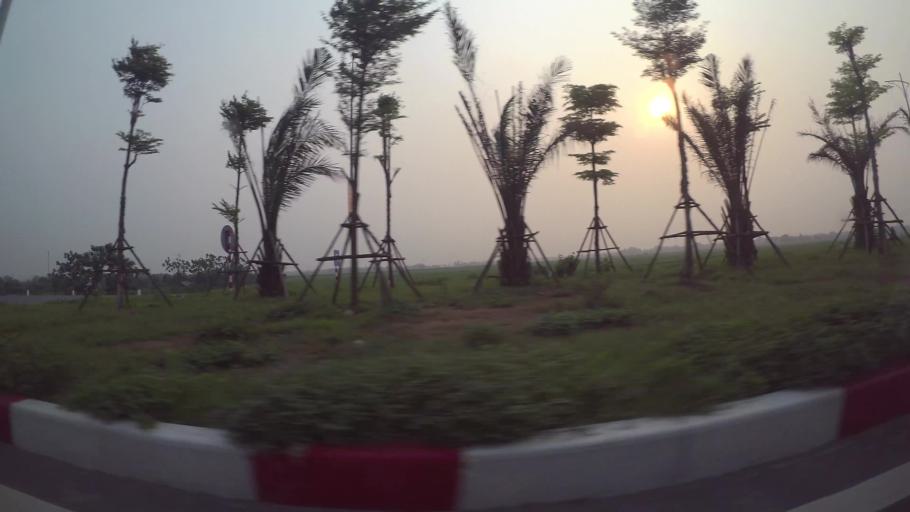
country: VN
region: Ha Noi
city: Kim Bai
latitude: 20.8783
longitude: 105.8007
